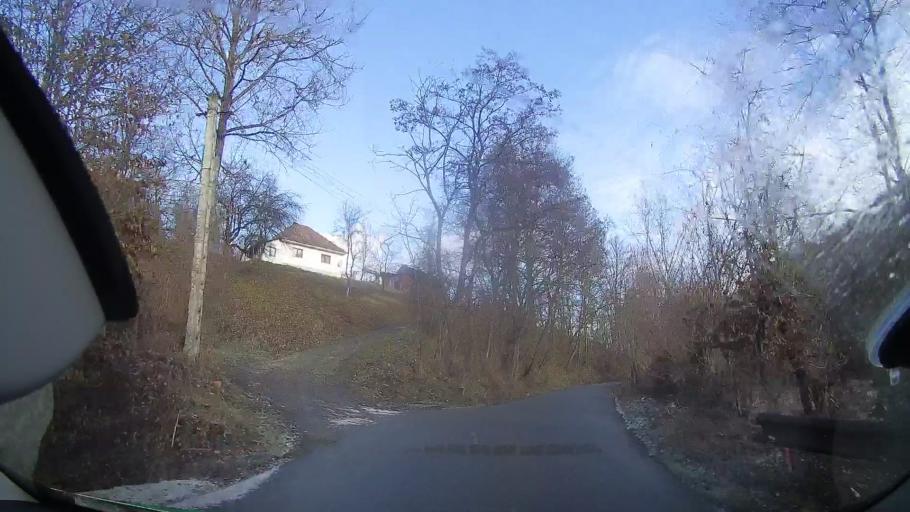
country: RO
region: Alba
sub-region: Comuna Sohodol
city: Sohodol
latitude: 46.3405
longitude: 23.0131
